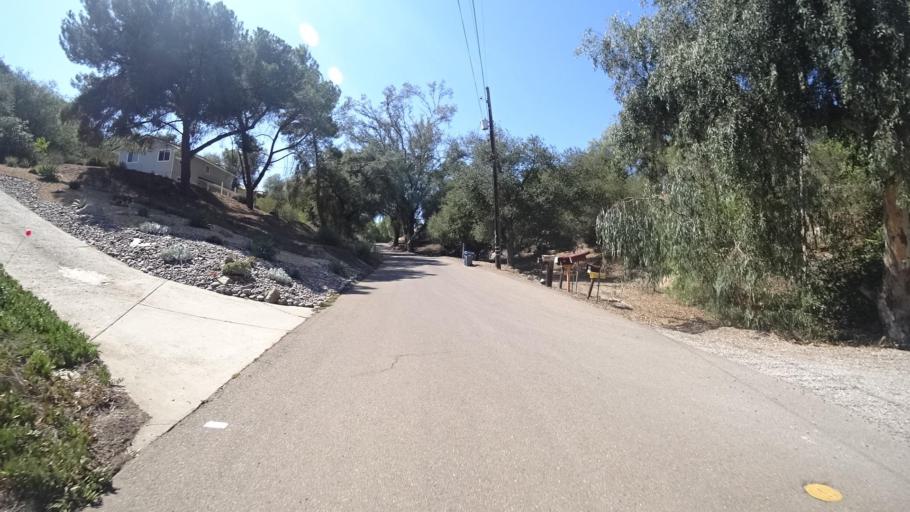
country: US
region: California
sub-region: San Diego County
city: Crest
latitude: 32.8093
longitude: -116.8620
